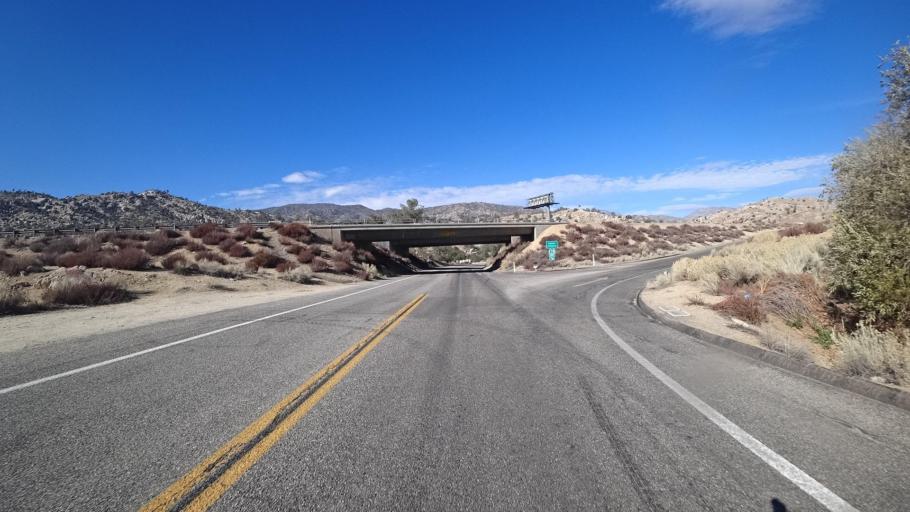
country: US
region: California
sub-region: Kern County
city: Lake Isabella
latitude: 35.6111
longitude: -118.4893
